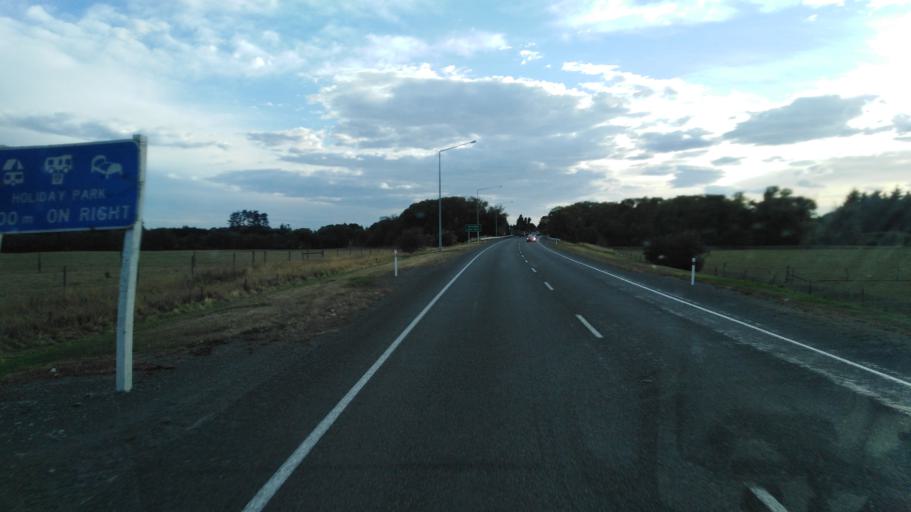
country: NZ
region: Canterbury
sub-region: Waimakariri District
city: Kaiapoi
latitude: -43.3564
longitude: 172.6579
